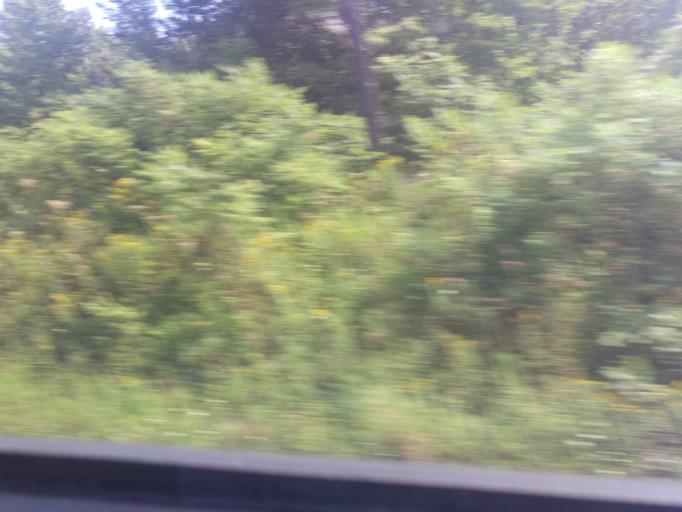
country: US
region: New York
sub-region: Jefferson County
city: Alexandria Bay
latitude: 44.4505
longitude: -75.9360
